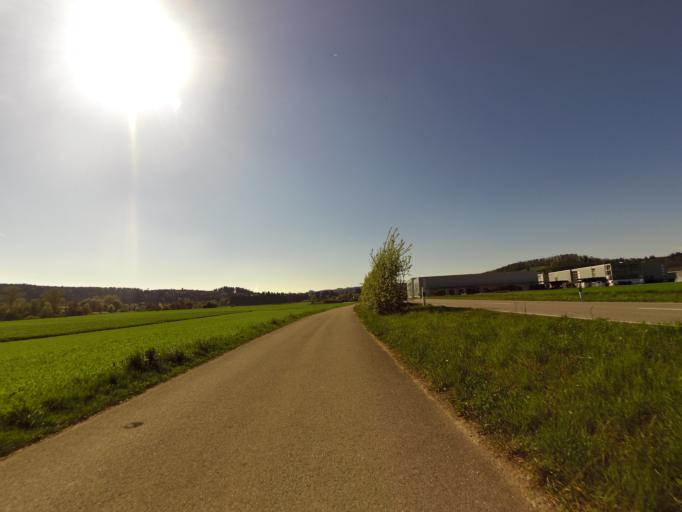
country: CH
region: Aargau
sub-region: Bezirk Zurzach
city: Bad Zurzach
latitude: 47.6155
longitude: 8.2798
